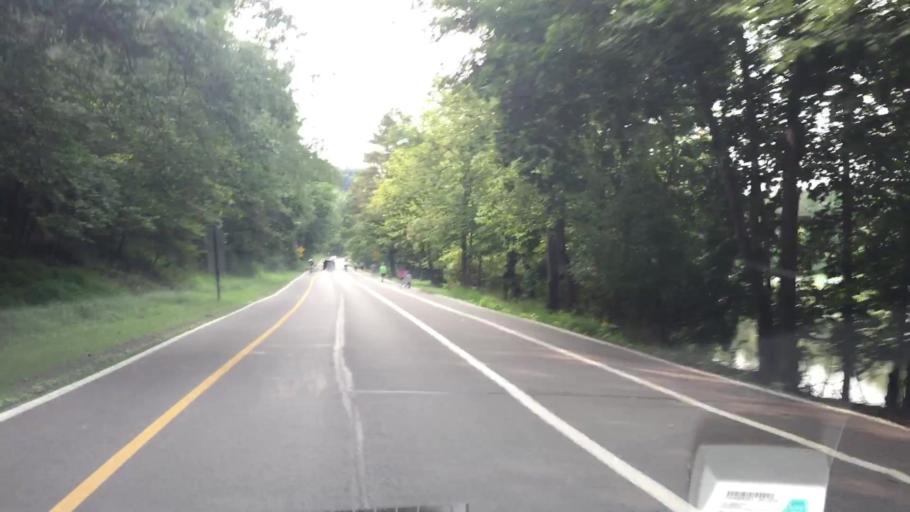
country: US
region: Pennsylvania
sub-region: Allegheny County
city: Gibsonia
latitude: 40.6035
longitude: -80.0082
